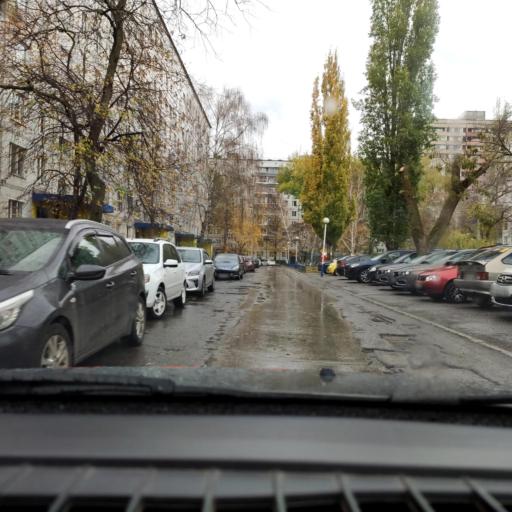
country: RU
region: Samara
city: Tol'yatti
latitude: 53.5085
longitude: 49.2645
